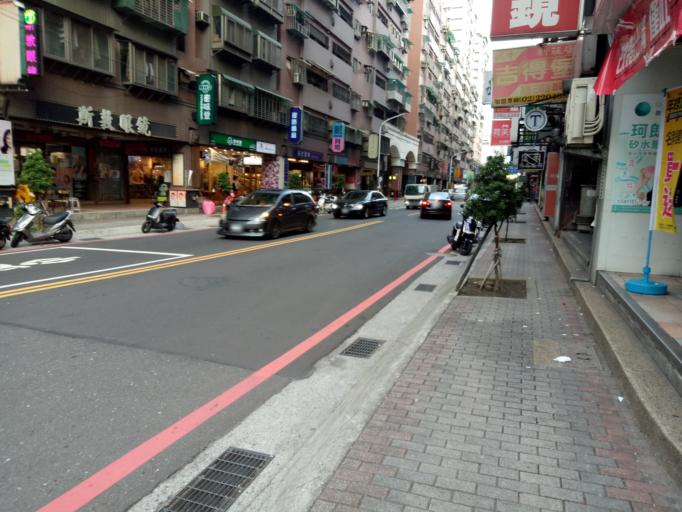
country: TW
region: Taipei
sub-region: Taipei
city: Banqiao
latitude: 25.0491
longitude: 121.4450
